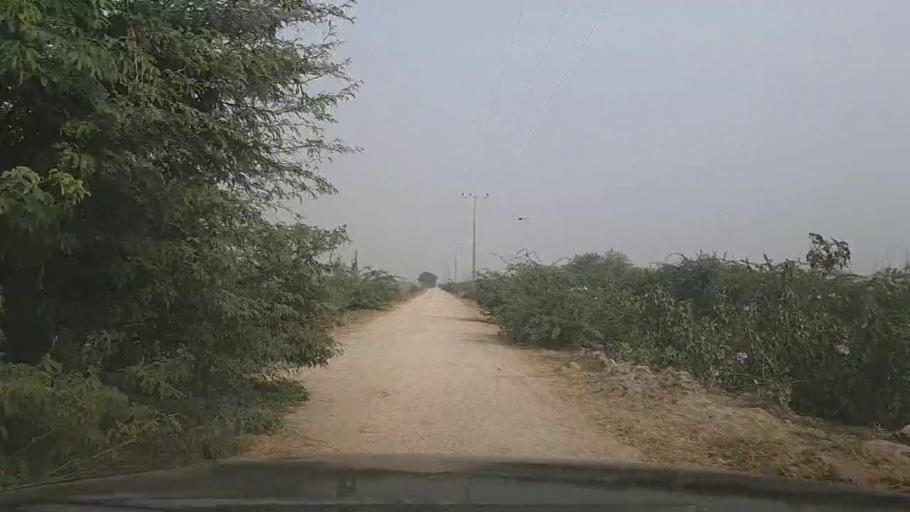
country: PK
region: Sindh
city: Mirpur Sakro
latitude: 24.5650
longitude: 67.7842
